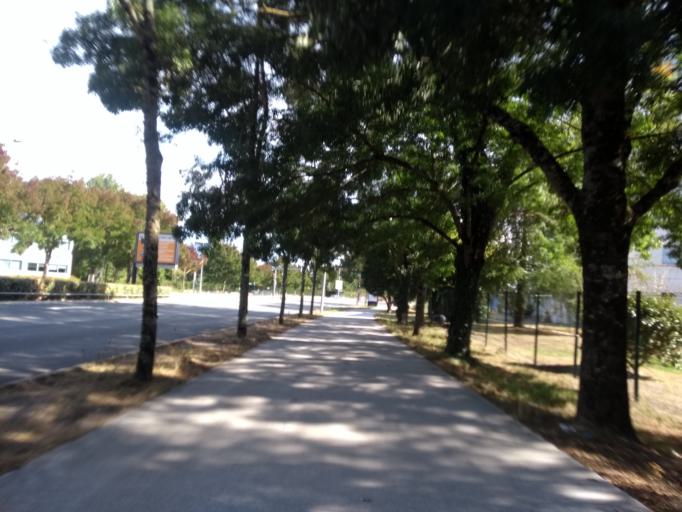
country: FR
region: Aquitaine
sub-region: Departement de la Gironde
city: Le Bouscat
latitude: 44.8905
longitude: -0.5628
